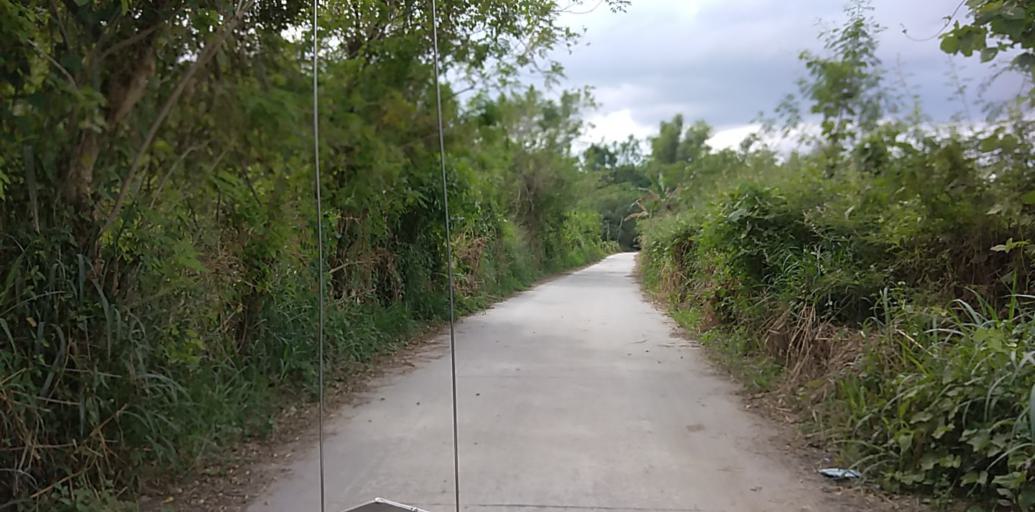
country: PH
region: Central Luzon
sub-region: Province of Pampanga
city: Porac
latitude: 15.0587
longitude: 120.5333
